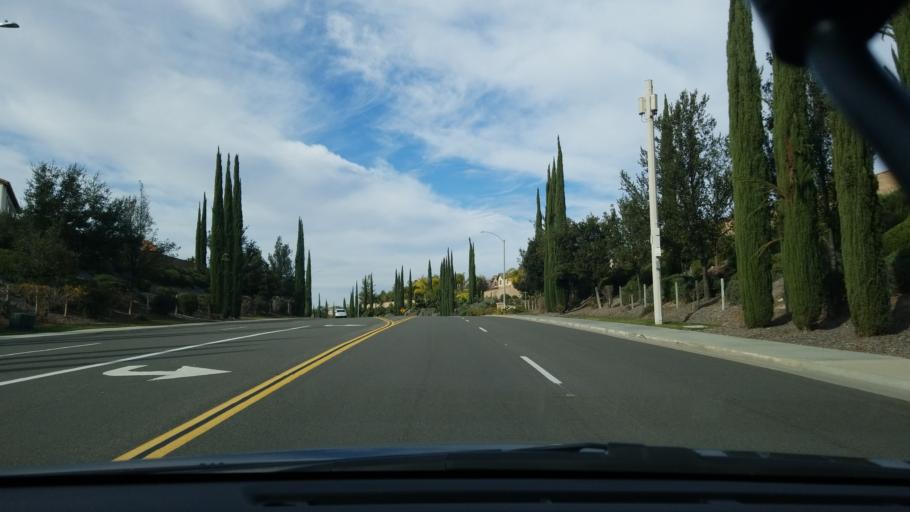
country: US
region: California
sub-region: Riverside County
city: Temecula
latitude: 33.4737
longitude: -117.0640
